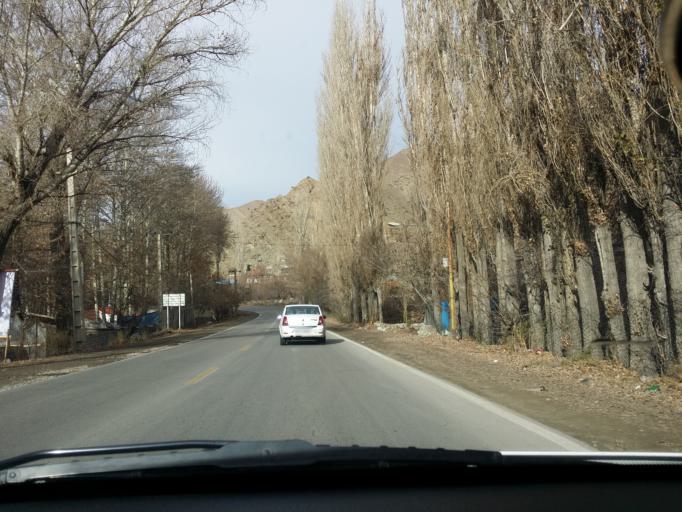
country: IR
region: Tehran
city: Tajrish
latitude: 36.0285
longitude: 51.2393
